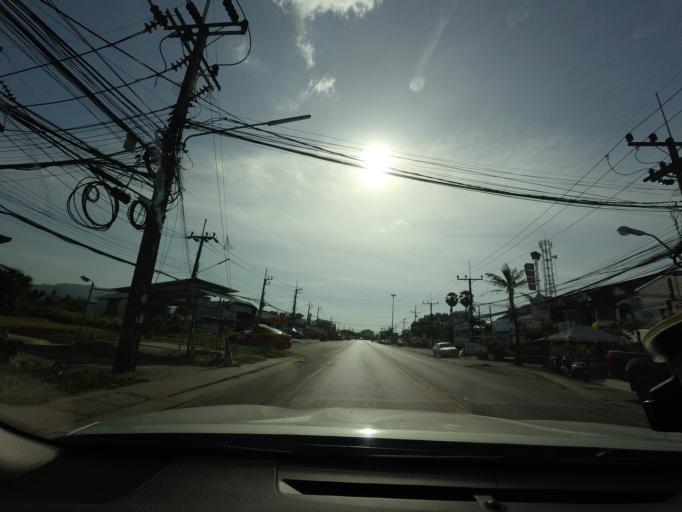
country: TH
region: Phuket
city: Thalang
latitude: 8.0268
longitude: 98.3304
